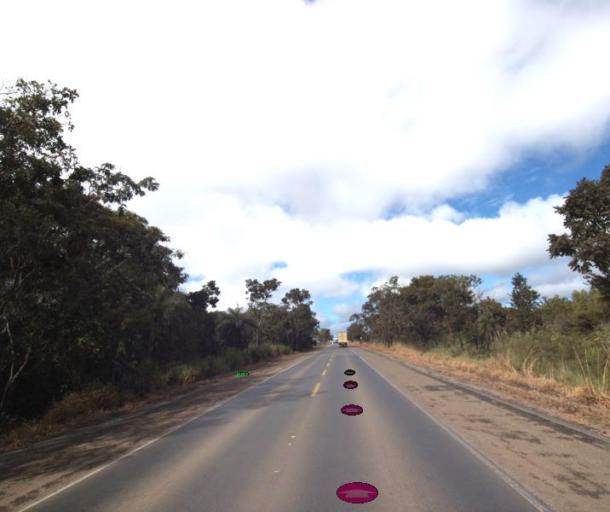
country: BR
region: Goias
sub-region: Uruacu
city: Uruacu
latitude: -14.7575
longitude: -49.2577
